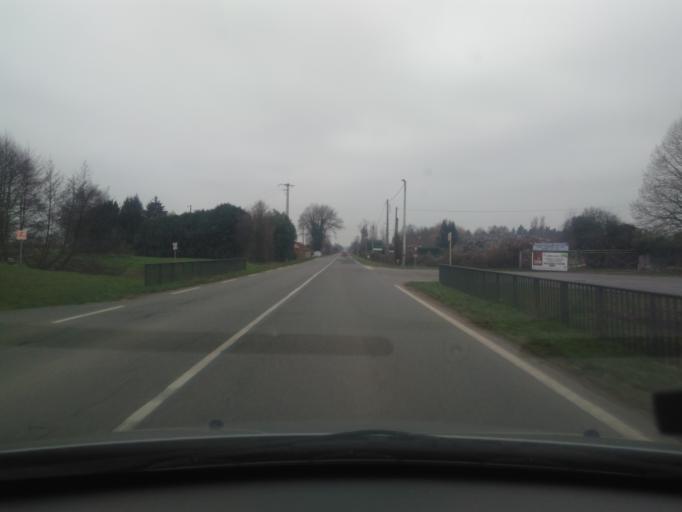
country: FR
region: Centre
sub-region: Departement du Cher
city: Charenton-du-Cher
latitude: 46.7313
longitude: 2.6304
